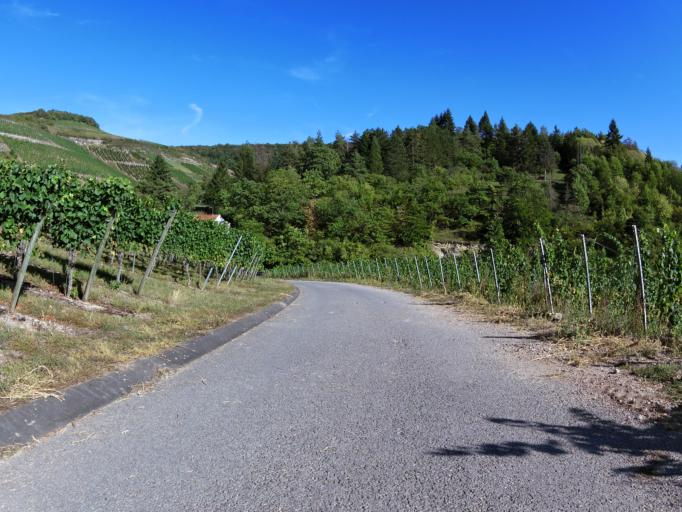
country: DE
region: Bavaria
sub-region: Regierungsbezirk Unterfranken
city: Erlabrunn
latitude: 49.8601
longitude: 9.8565
